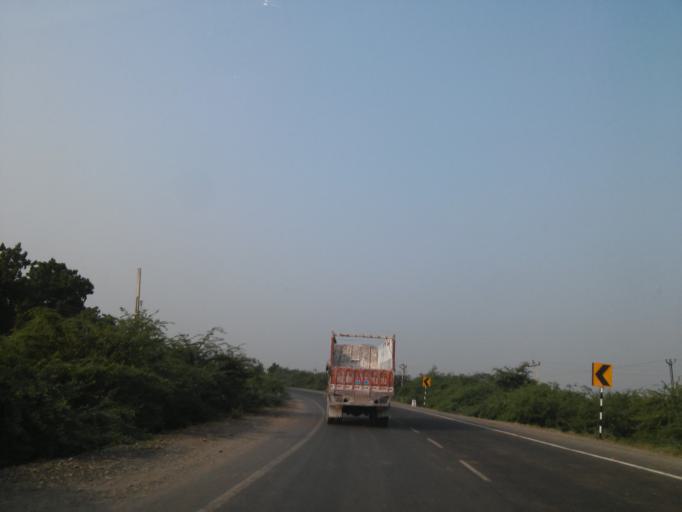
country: IN
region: Gujarat
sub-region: Kachchh
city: Anjar
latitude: 23.3123
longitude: 70.1195
